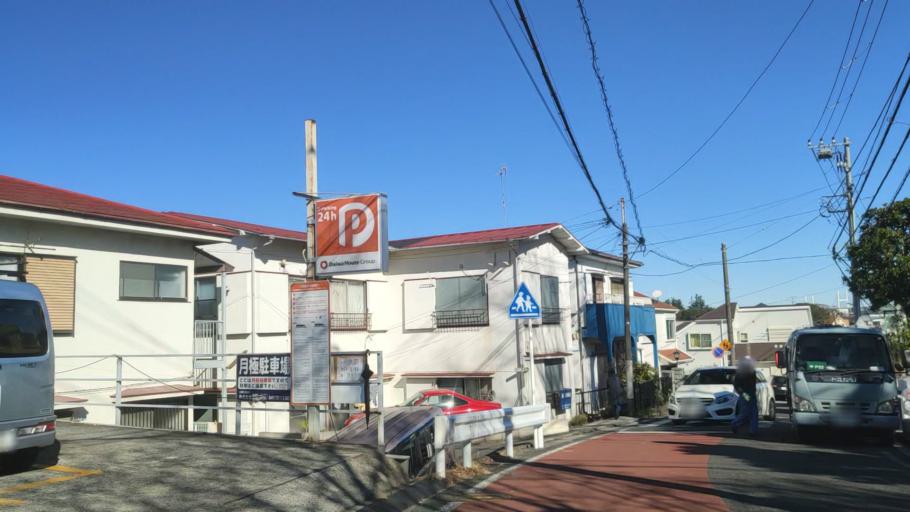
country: JP
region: Kanagawa
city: Yokohama
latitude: 35.4312
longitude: 139.6451
